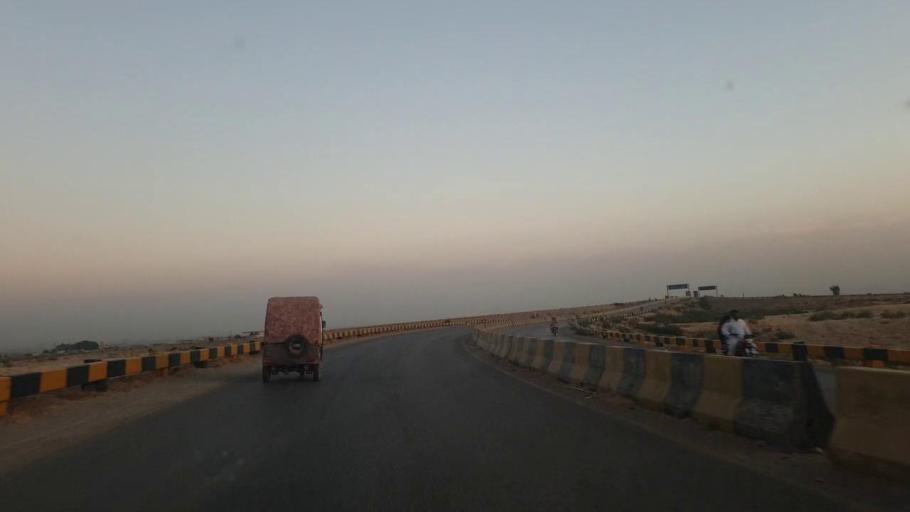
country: PK
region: Sindh
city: Jamshoro
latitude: 25.4038
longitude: 68.2713
